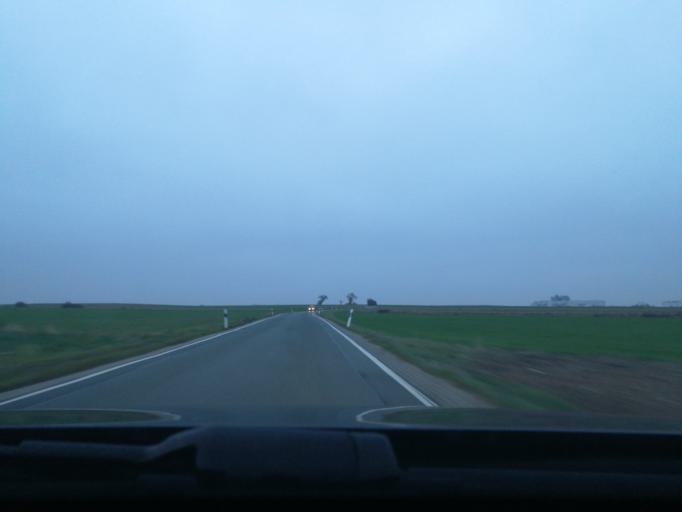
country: DE
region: Bavaria
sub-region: Regierungsbezirk Mittelfranken
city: Obermichelbach
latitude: 49.4943
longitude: 10.9291
